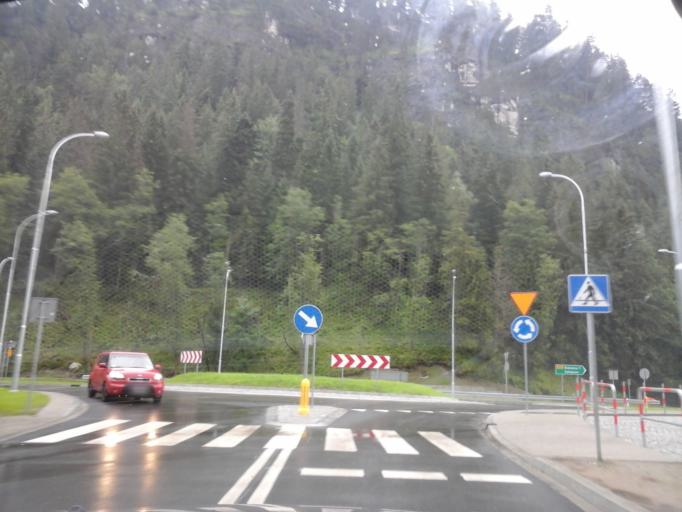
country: PL
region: Lesser Poland Voivodeship
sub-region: Powiat tatrzanski
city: Bukowina Tatrzanska
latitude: 49.2636
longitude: 20.1148
